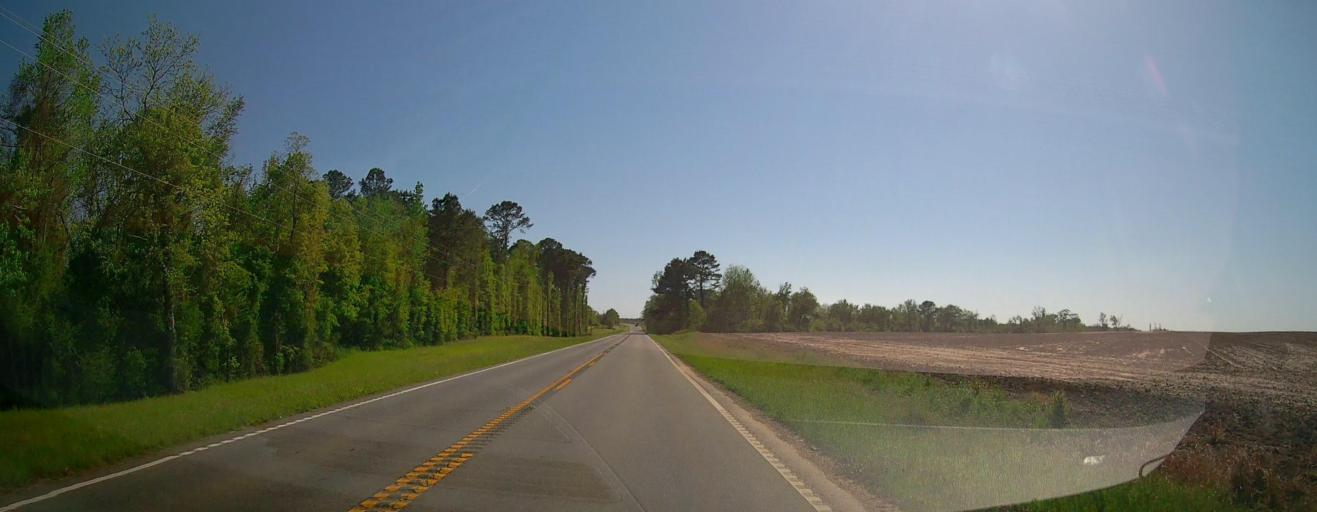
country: US
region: Georgia
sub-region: Pulaski County
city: Hawkinsville
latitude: 32.2110
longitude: -83.4870
